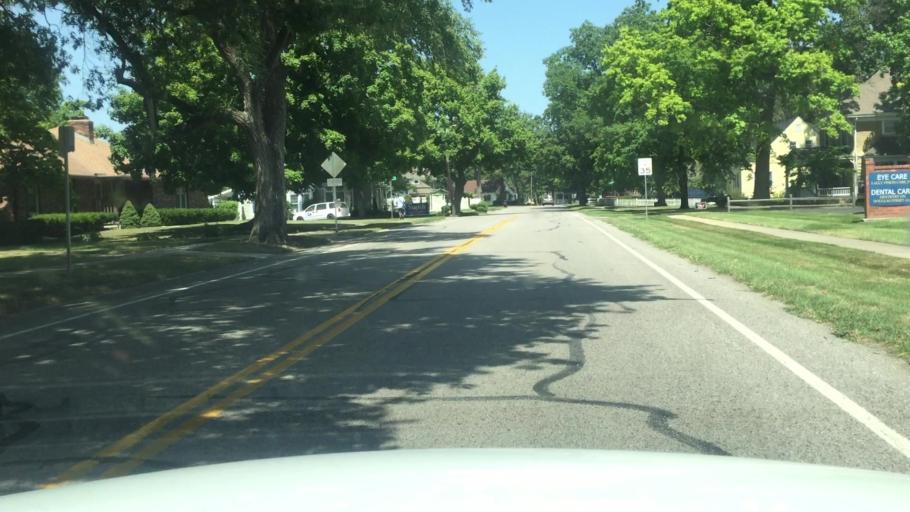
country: US
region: Missouri
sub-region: Jackson County
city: Lees Summit
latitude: 38.9166
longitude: -94.3790
